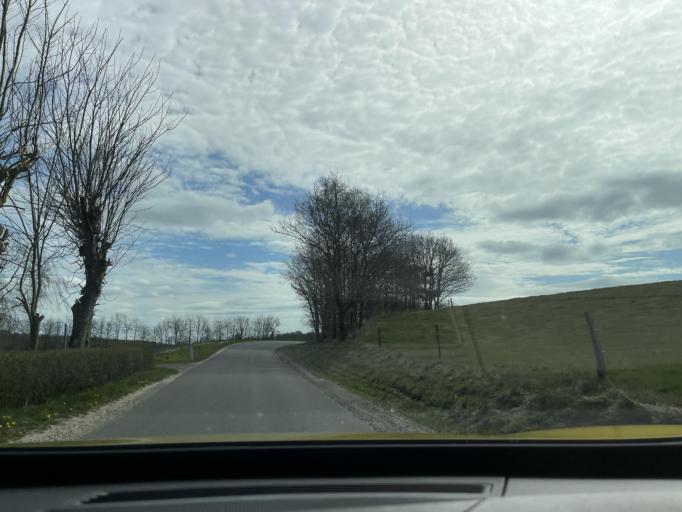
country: DK
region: Central Jutland
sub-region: Favrskov Kommune
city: Hinnerup
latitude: 56.3033
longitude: 10.1017
